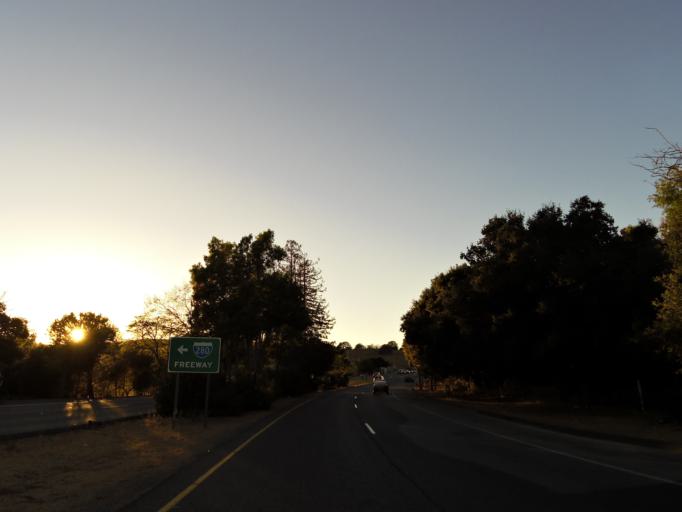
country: US
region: California
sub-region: Santa Clara County
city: Stanford
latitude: 37.4054
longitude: -122.1533
